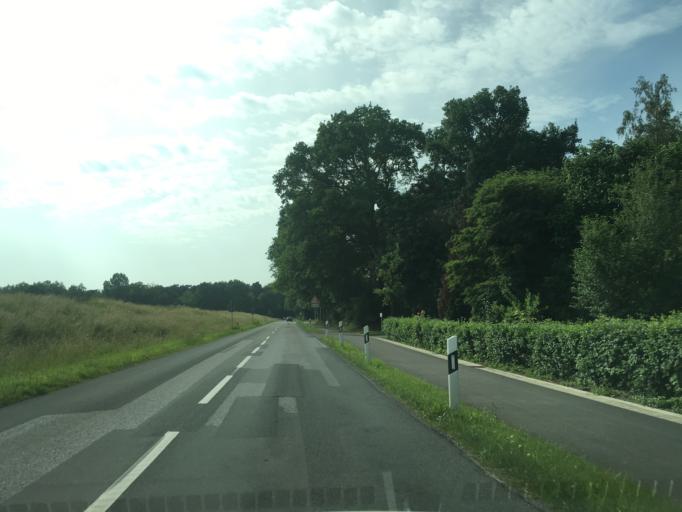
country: DE
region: North Rhine-Westphalia
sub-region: Regierungsbezirk Munster
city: Senden
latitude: 51.8692
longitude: 7.5489
